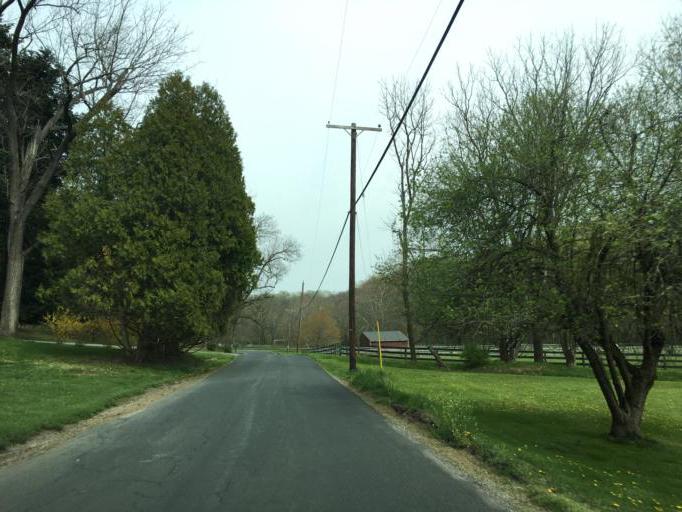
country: US
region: Maryland
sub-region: Baltimore County
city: Hunt Valley
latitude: 39.5684
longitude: -76.6185
